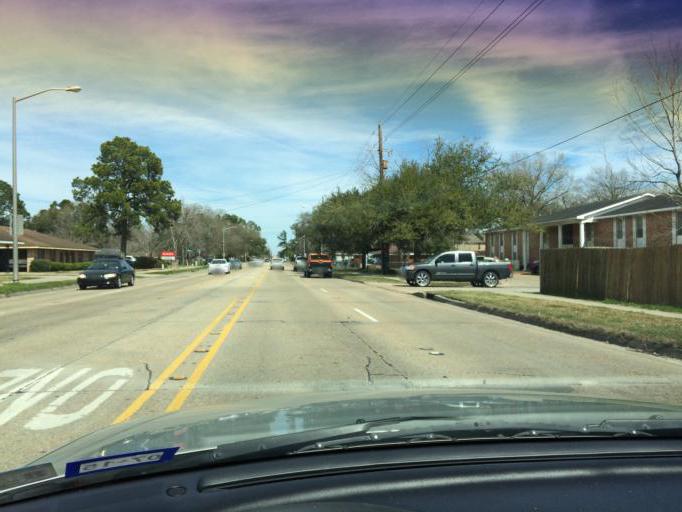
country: US
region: Louisiana
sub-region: Lafayette Parish
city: Scott
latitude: 30.2027
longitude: -92.0635
